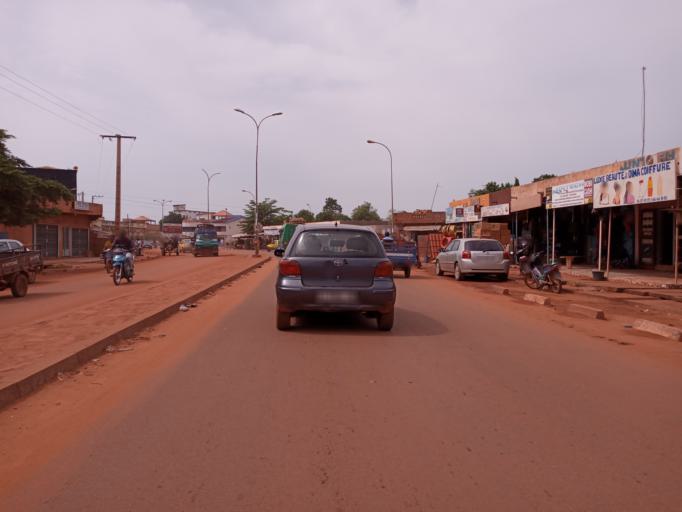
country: ML
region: Bamako
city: Bamako
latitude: 12.5496
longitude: -7.9990
